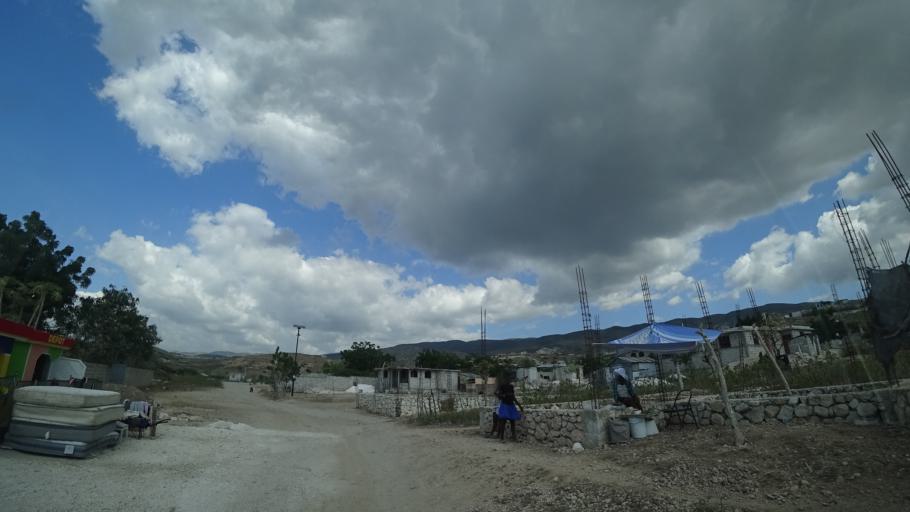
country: HT
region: Ouest
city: Cabaret
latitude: 18.6775
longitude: -72.3162
